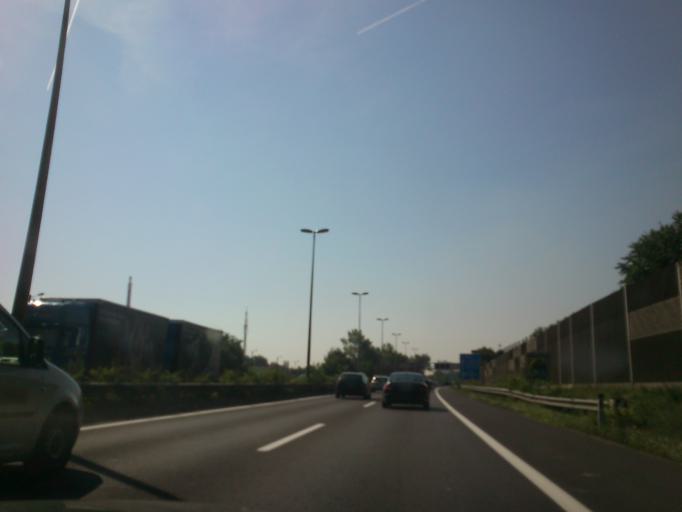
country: AT
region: Upper Austria
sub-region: Linz Stadt
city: Linz
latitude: 48.3078
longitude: 14.3123
